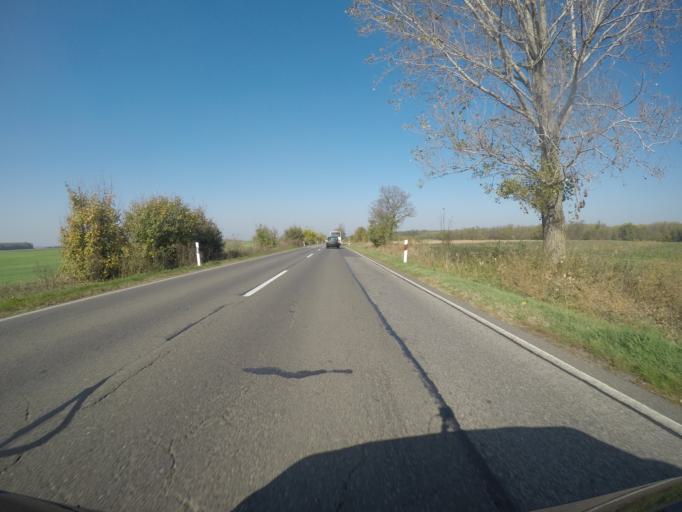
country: HU
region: Tolna
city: Szedres
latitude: 46.5016
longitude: 18.6699
